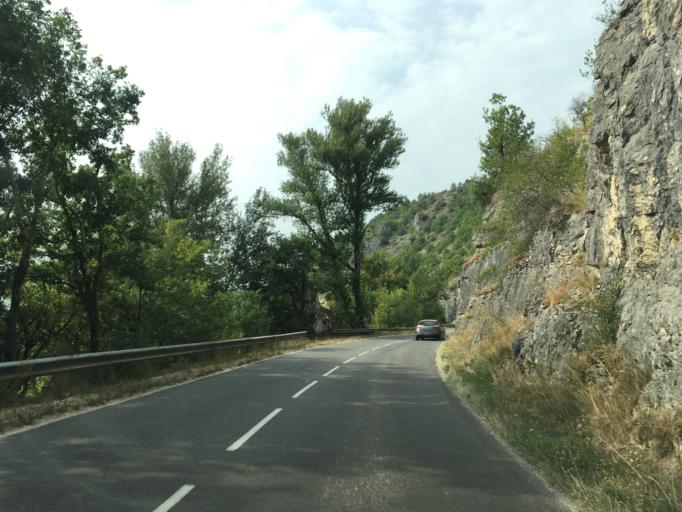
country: FR
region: Midi-Pyrenees
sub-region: Departement du Lot
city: Souillac
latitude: 44.8728
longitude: 1.4973
